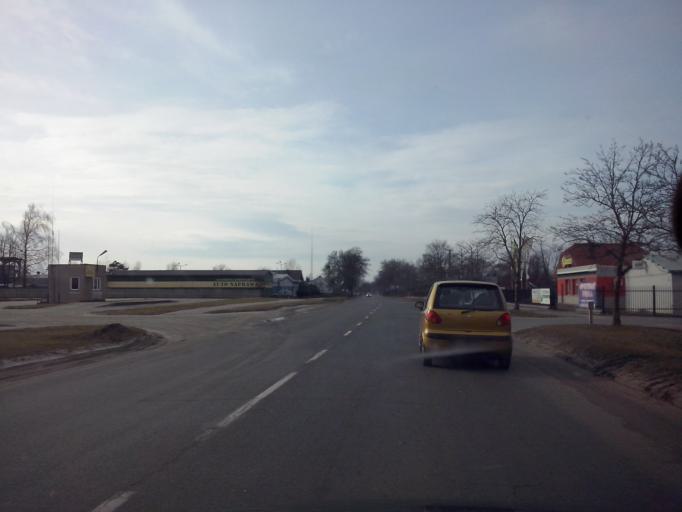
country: PL
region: Lublin Voivodeship
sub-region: Powiat bilgorajski
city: Bilgoraj
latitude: 50.5224
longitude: 22.6948
